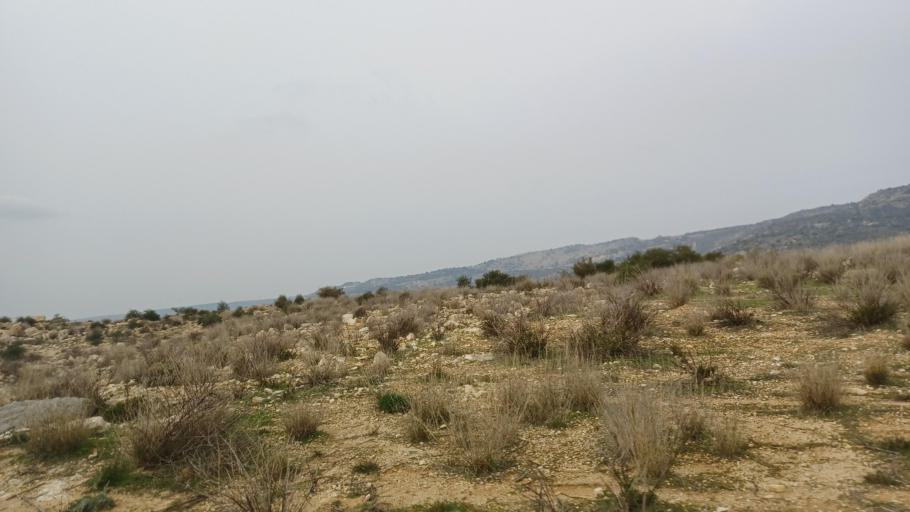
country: CY
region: Limassol
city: Pachna
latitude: 34.7541
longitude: 32.7403
